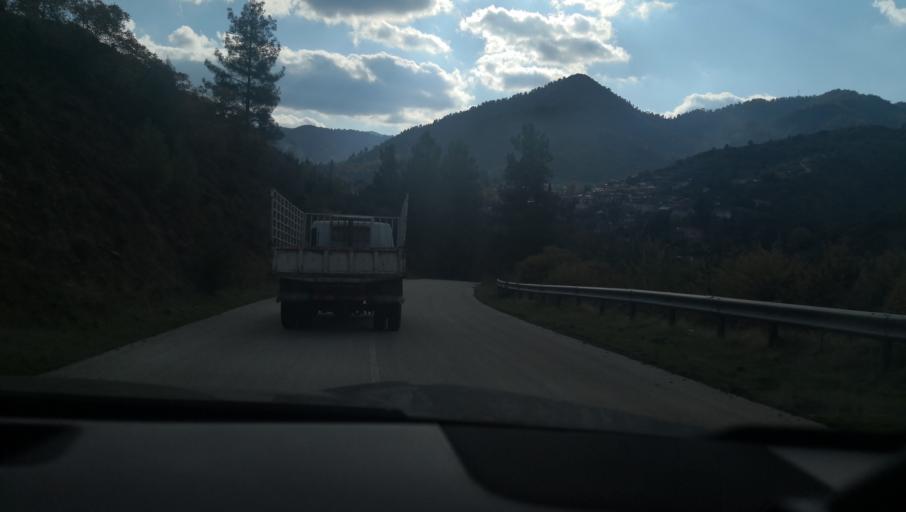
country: CY
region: Lefkosia
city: Lefka
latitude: 35.0461
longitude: 32.7371
